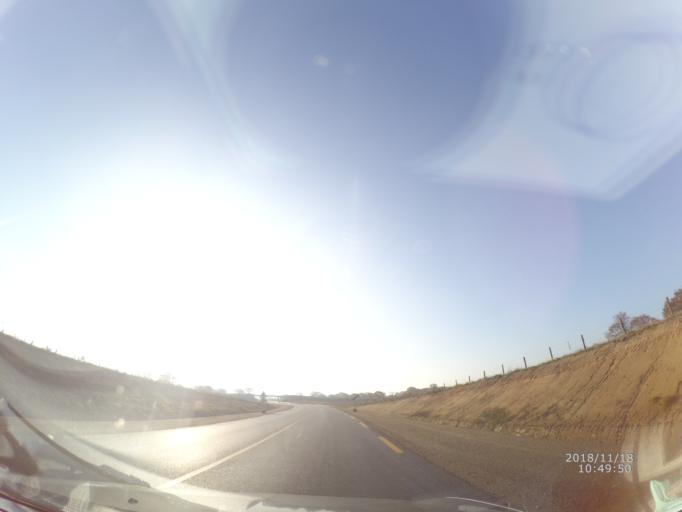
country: FR
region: Pays de la Loire
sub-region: Departement de la Loire-Atlantique
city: Vue
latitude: 47.2022
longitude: -1.9189
